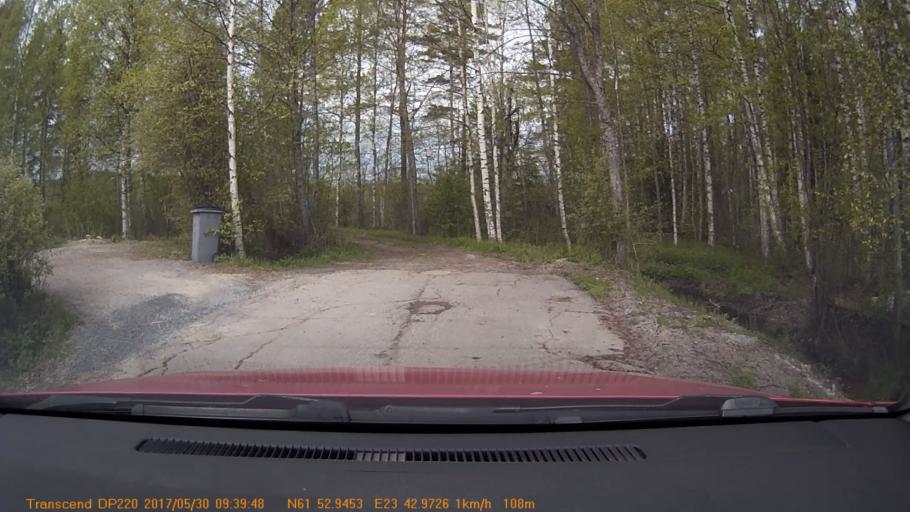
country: FI
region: Pirkanmaa
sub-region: Tampere
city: Kuru
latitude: 61.8824
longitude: 23.7163
